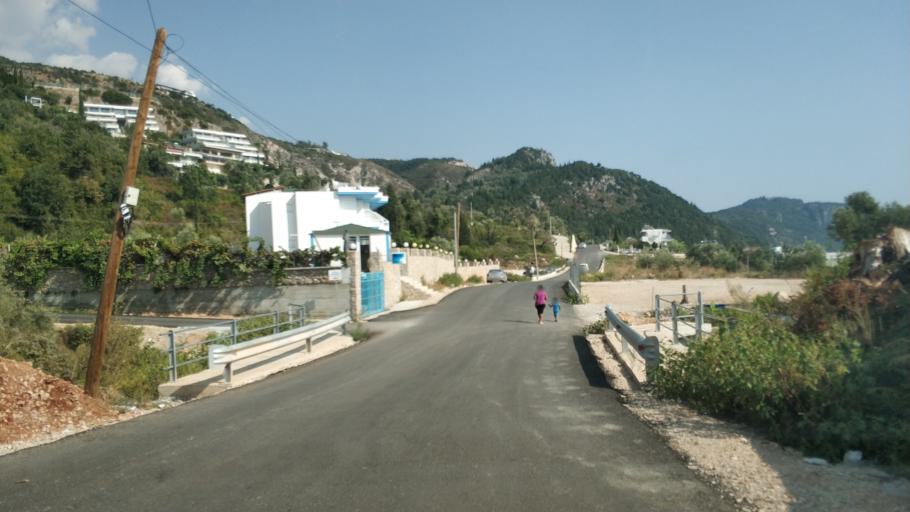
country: AL
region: Vlore
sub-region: Rrethi i Vlores
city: Vranisht
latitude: 40.1451
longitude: 19.6356
